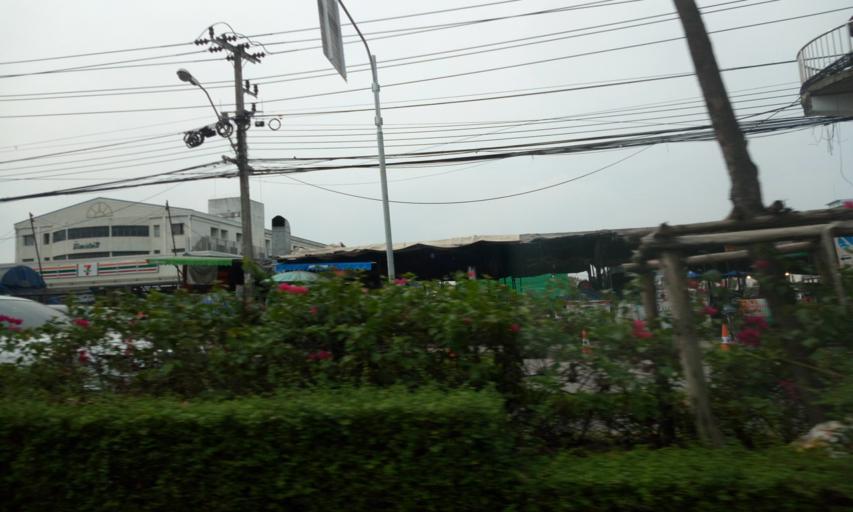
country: TH
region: Bangkok
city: Saphan Sung
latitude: 13.7222
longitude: 100.7187
